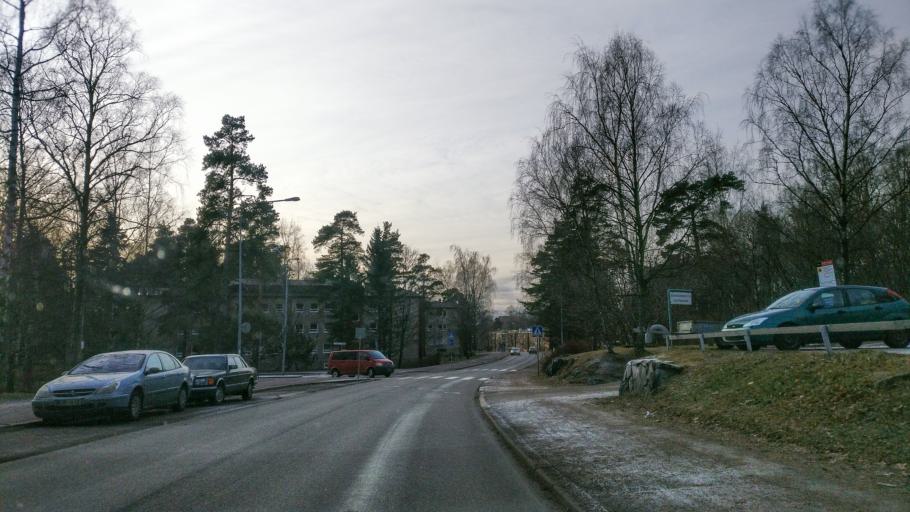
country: FI
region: Uusimaa
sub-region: Helsinki
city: Vantaa
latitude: 60.1992
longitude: 25.0583
